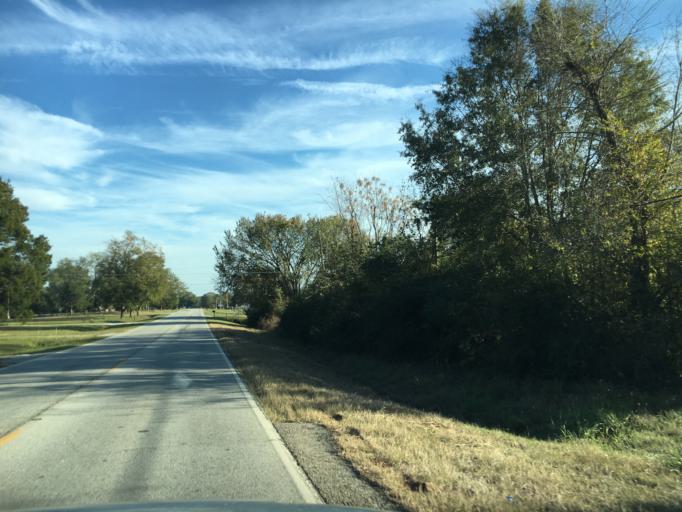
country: US
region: Georgia
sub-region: Elbert County
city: Elberton
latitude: 34.0555
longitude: -82.8243
